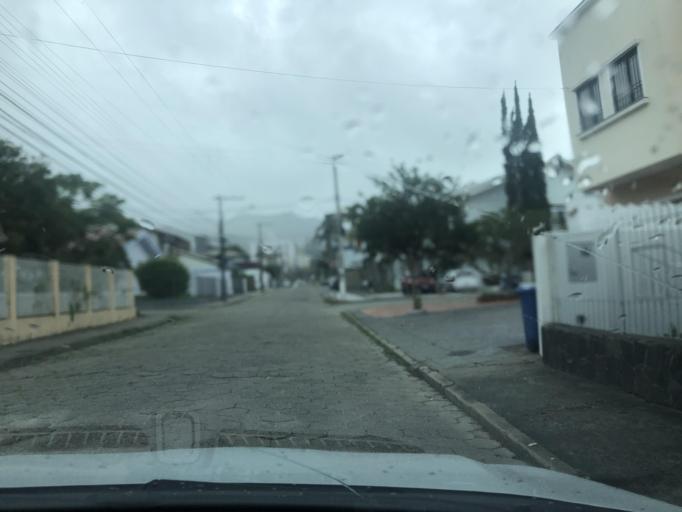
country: BR
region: Santa Catarina
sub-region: Florianopolis
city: Corrego Grande
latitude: -27.5975
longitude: -48.5129
